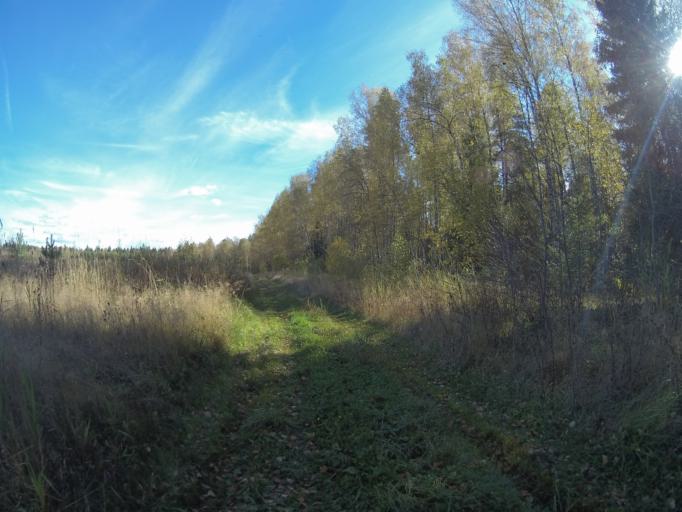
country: RU
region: Vladimir
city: Kommunar
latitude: 56.0336
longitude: 40.4913
